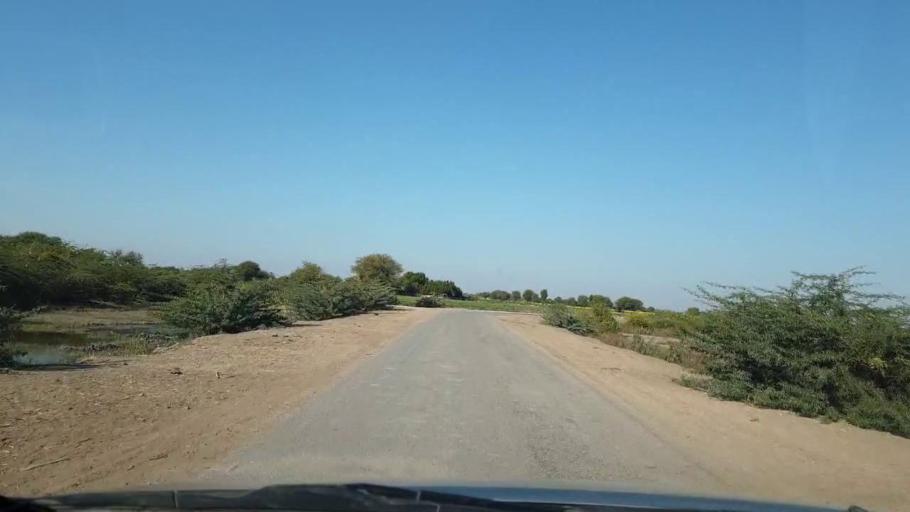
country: PK
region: Sindh
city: Jhol
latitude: 25.8258
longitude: 68.9482
